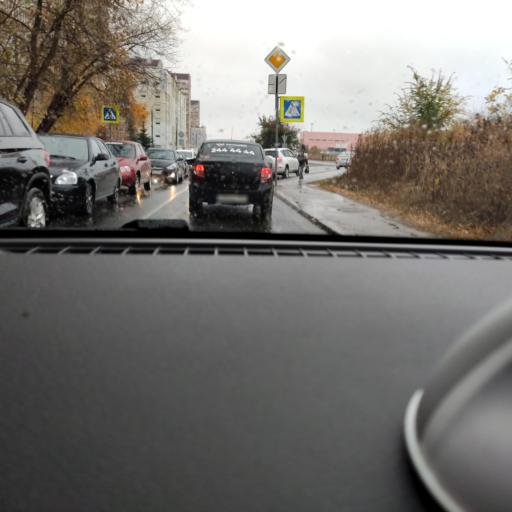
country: RU
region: Samara
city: Samara
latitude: 53.2106
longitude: 50.2029
